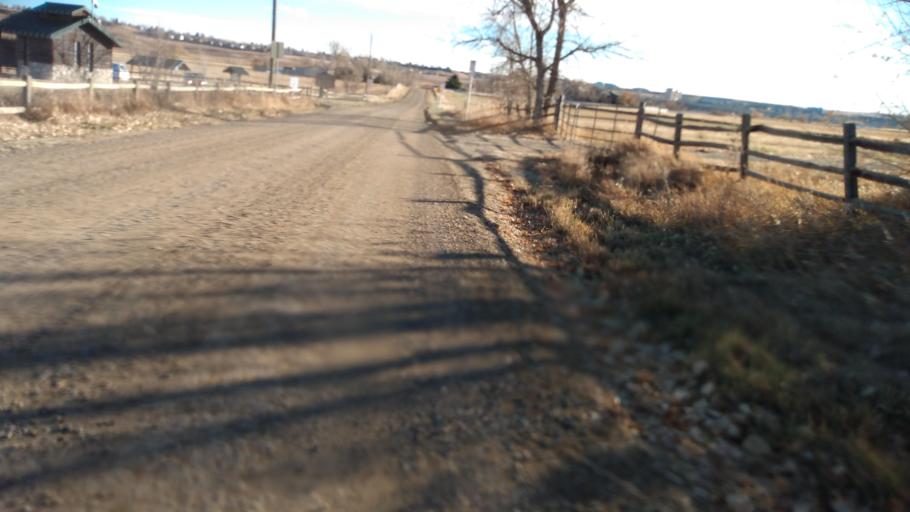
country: US
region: Colorado
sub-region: Boulder County
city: Louisville
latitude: 39.9481
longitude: -105.1107
